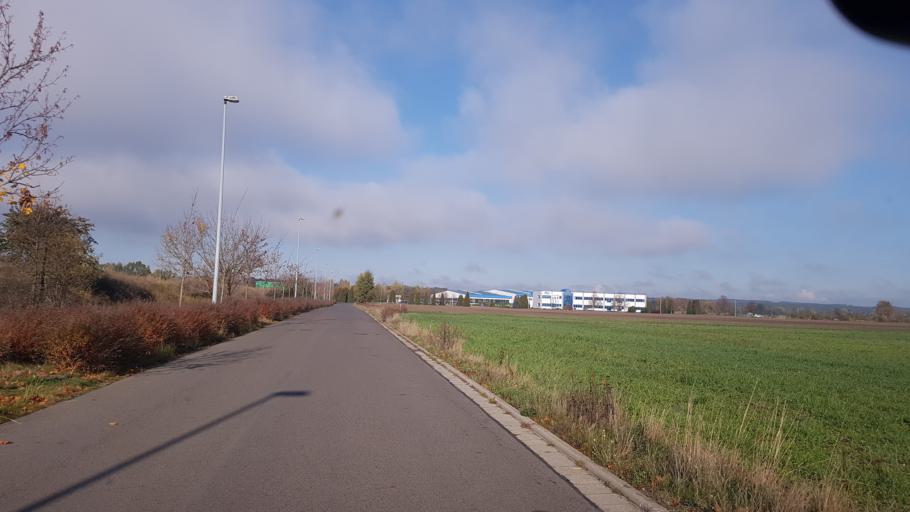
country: DE
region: Brandenburg
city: Elsterwerda
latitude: 51.4612
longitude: 13.5483
